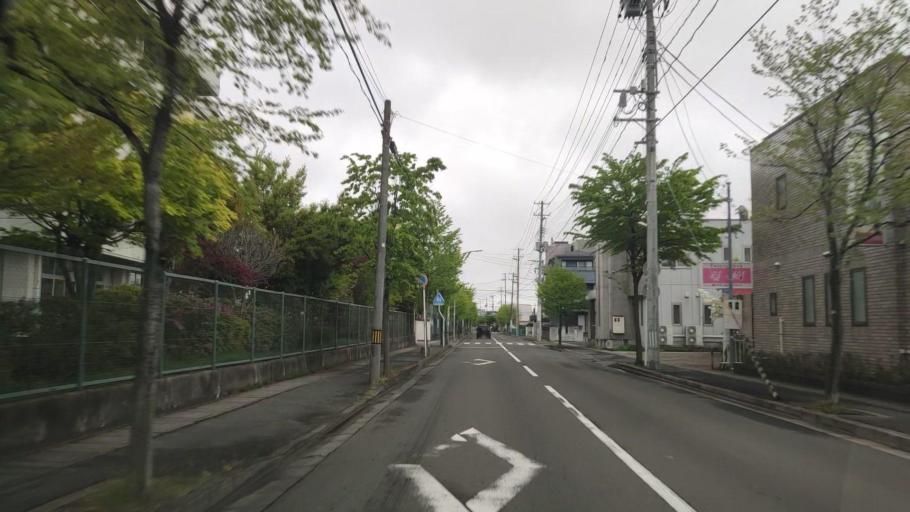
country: JP
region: Miyagi
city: Sendai
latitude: 38.2180
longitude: 140.8627
